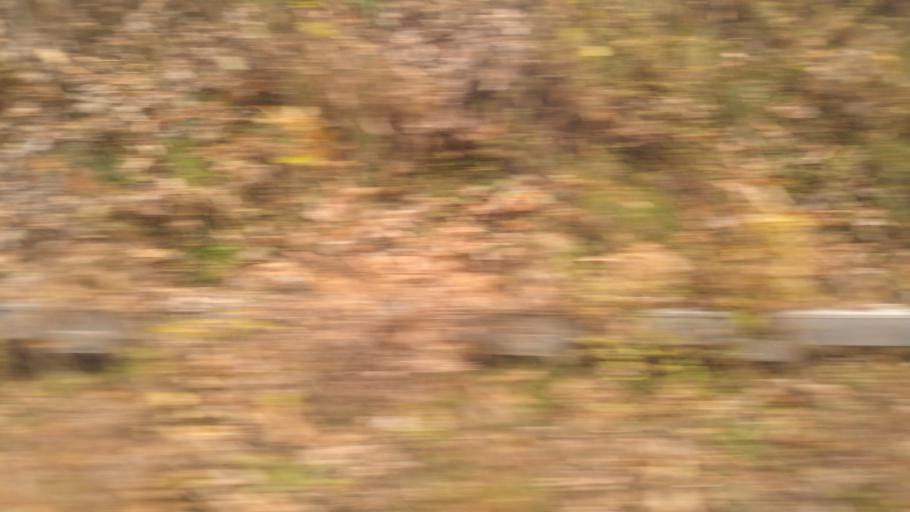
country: JP
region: Nagano
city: Nagano-shi
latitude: 36.4961
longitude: 138.0990
